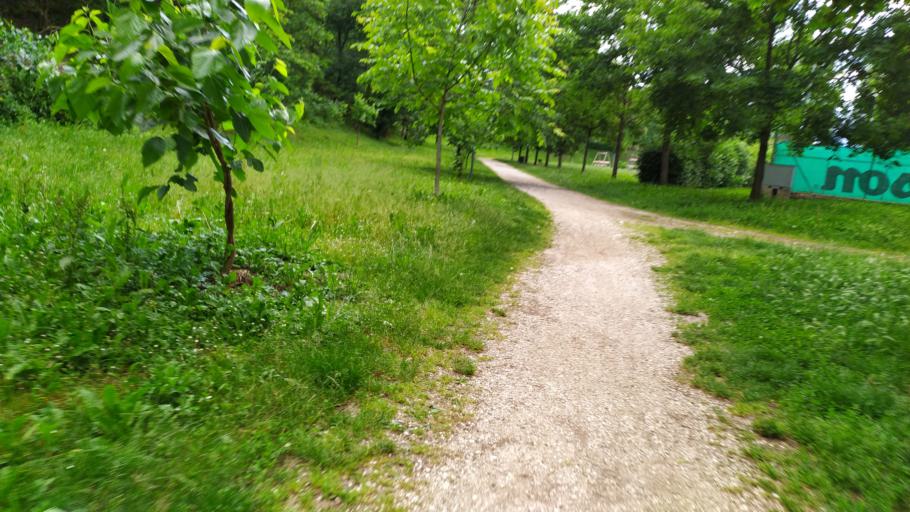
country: IT
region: Veneto
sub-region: Provincia di Vicenza
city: Malo
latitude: 45.6543
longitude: 11.4076
